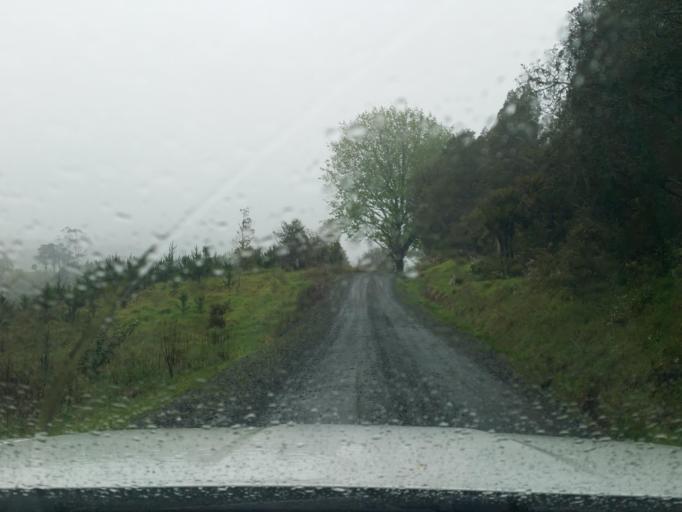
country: NZ
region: Northland
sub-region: Kaipara District
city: Dargaville
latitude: -35.7503
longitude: 173.9588
